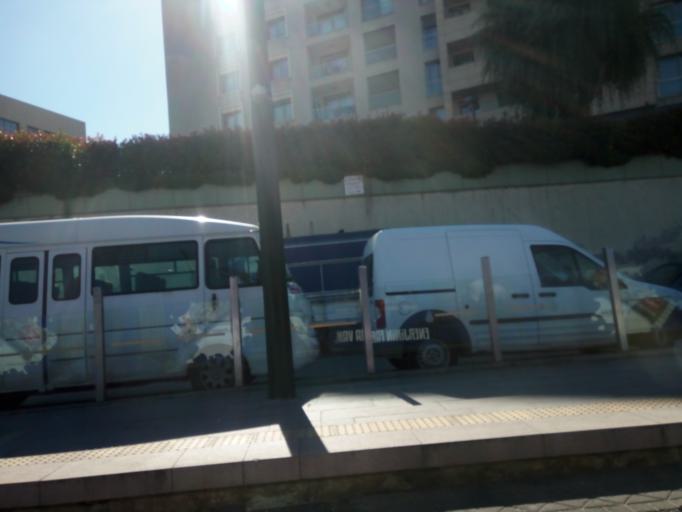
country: TR
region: Istanbul
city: Zeytinburnu
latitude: 41.0101
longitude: 28.9091
